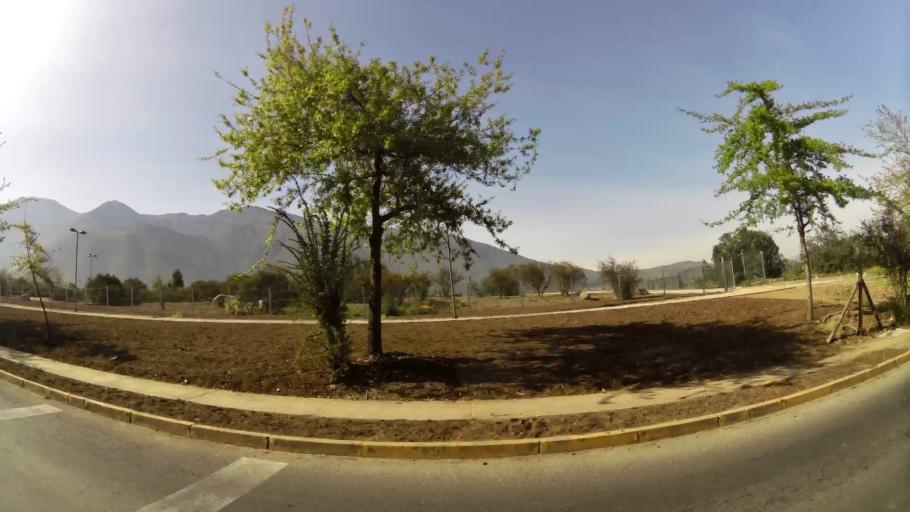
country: CL
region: Santiago Metropolitan
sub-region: Provincia de Santiago
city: Villa Presidente Frei, Nunoa, Santiago, Chile
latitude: -33.5022
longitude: -70.5302
